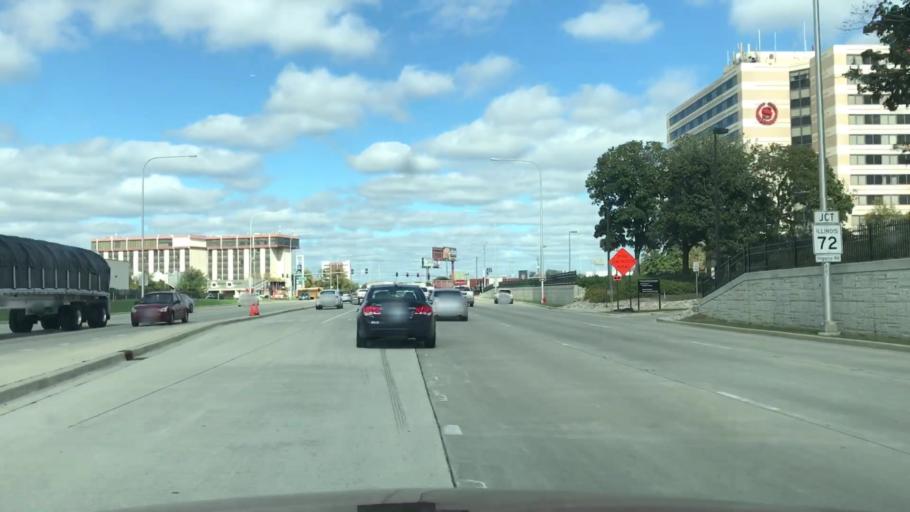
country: US
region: Illinois
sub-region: Cook County
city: Rosemont
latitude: 41.9960
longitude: -87.8845
